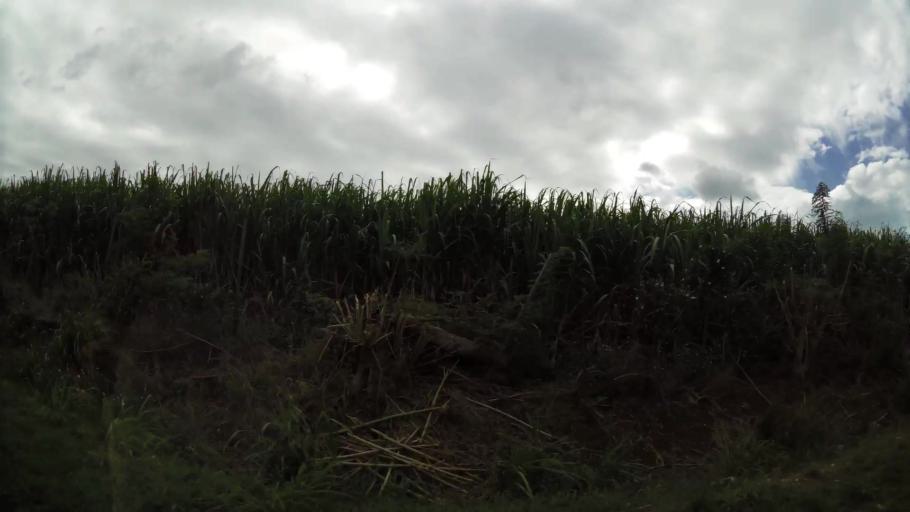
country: GP
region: Guadeloupe
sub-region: Guadeloupe
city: Sainte-Rose
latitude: 16.3242
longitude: -61.6992
